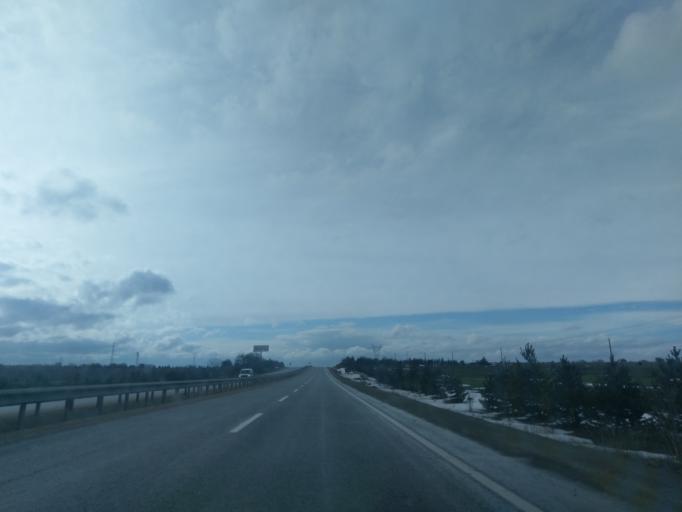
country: TR
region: Eskisehir
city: Inonu
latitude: 39.7201
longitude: 30.2183
